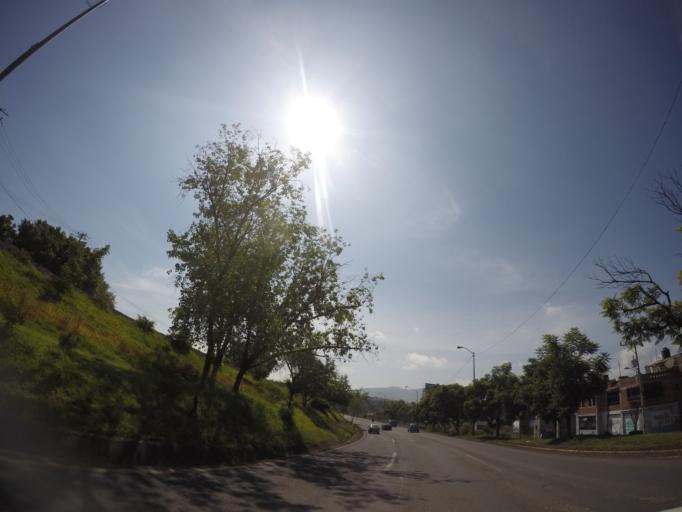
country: MX
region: Michoacan
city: Morelia
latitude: 19.7191
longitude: -101.1835
